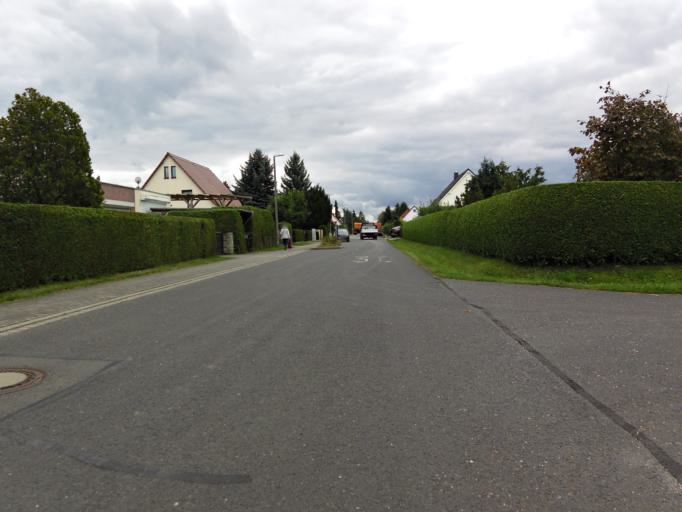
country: DE
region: Saxony
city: Grossposna
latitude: 51.2942
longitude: 12.4365
